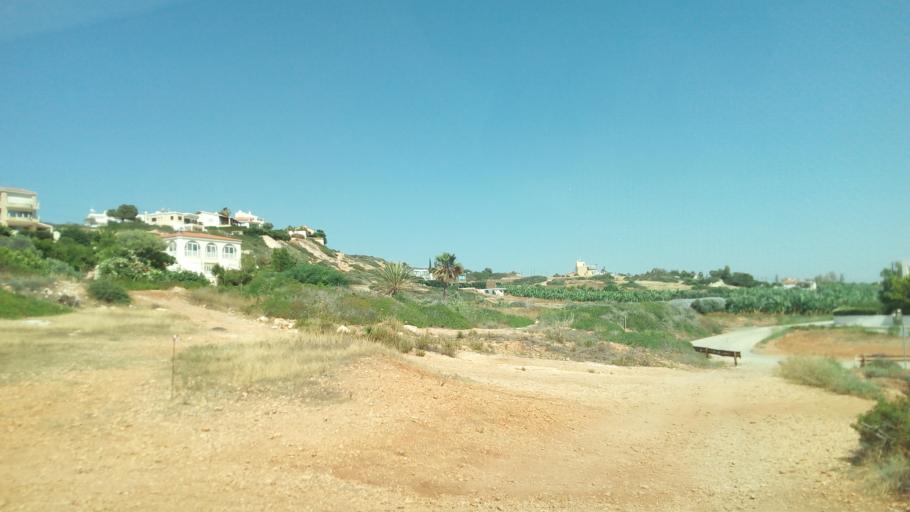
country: CY
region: Pafos
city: Pegeia
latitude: 34.8845
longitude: 32.3331
